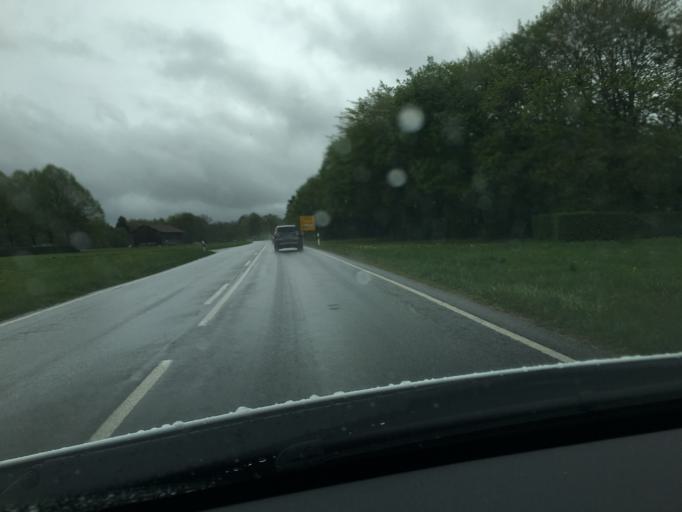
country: DE
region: Bavaria
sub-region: Upper Bavaria
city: Baierbrunn
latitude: 48.0167
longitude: 11.4820
